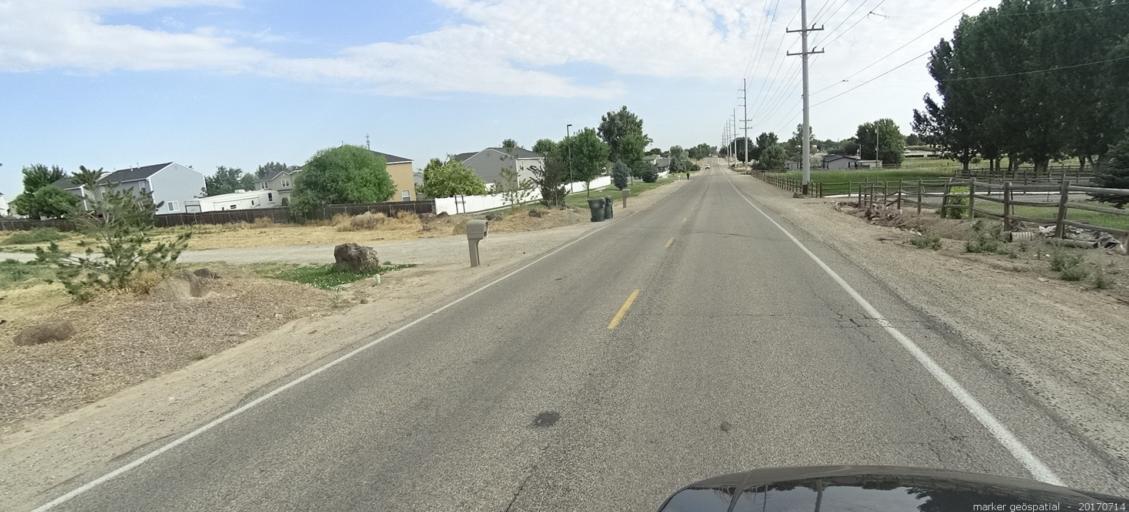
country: US
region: Idaho
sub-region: Ada County
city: Kuna
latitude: 43.4799
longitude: -116.4137
